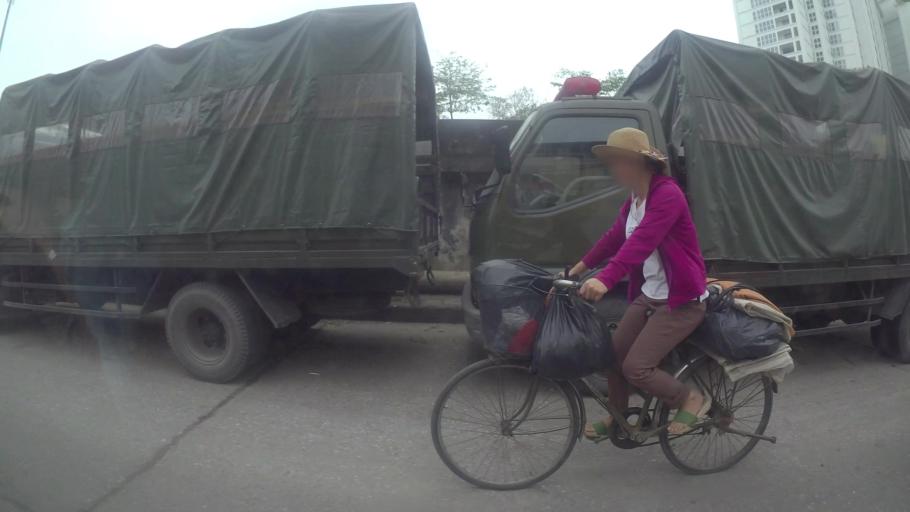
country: VN
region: Ha Noi
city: Hoan Kiem
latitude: 21.0447
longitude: 105.8466
